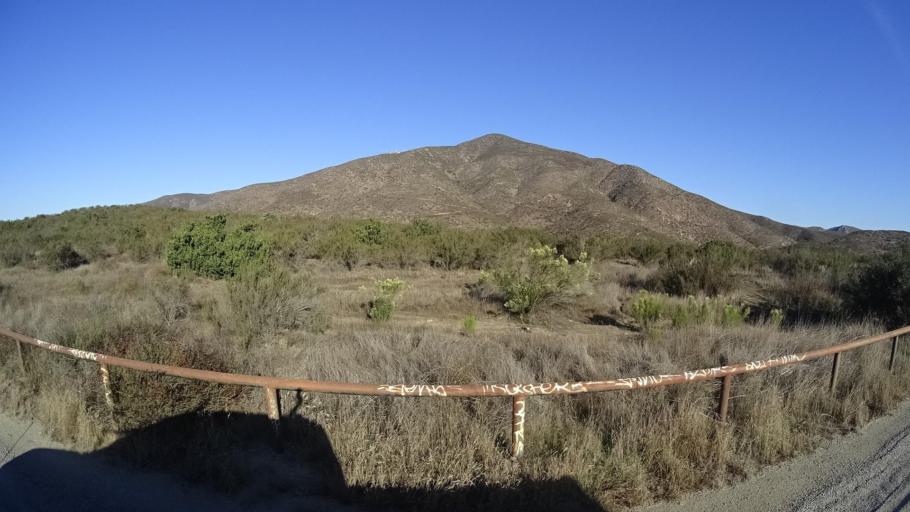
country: US
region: California
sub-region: San Diego County
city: Jamul
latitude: 32.6821
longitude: -116.9133
